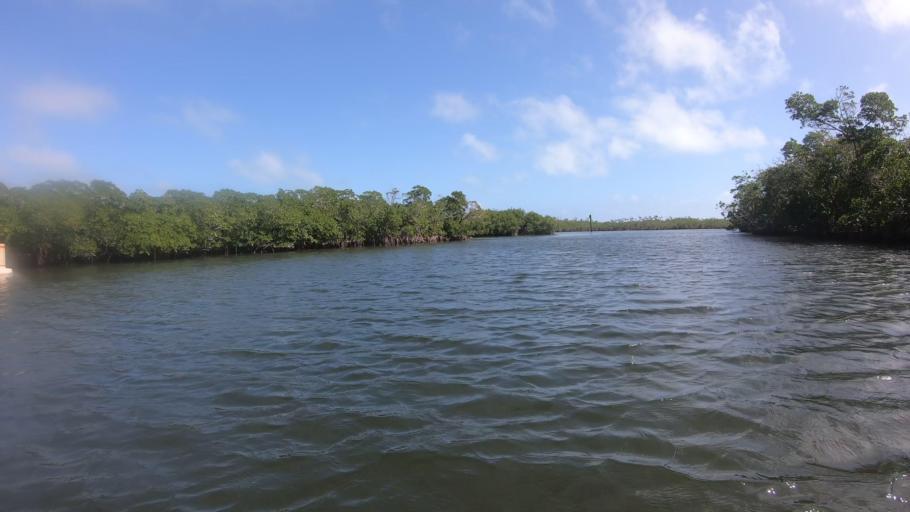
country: US
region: Florida
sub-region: Monroe County
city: Key Largo
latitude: 25.1217
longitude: -80.4035
